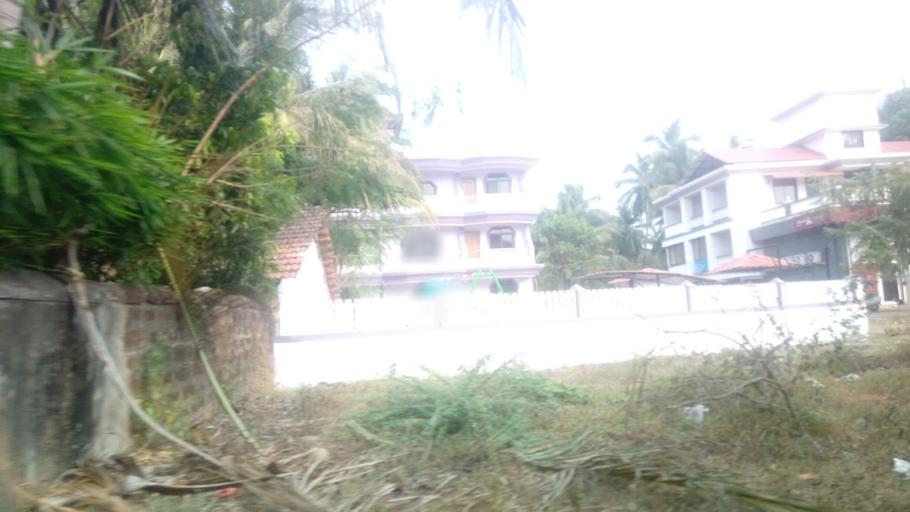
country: IN
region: Goa
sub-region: South Goa
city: Varca
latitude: 15.2301
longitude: 73.9440
